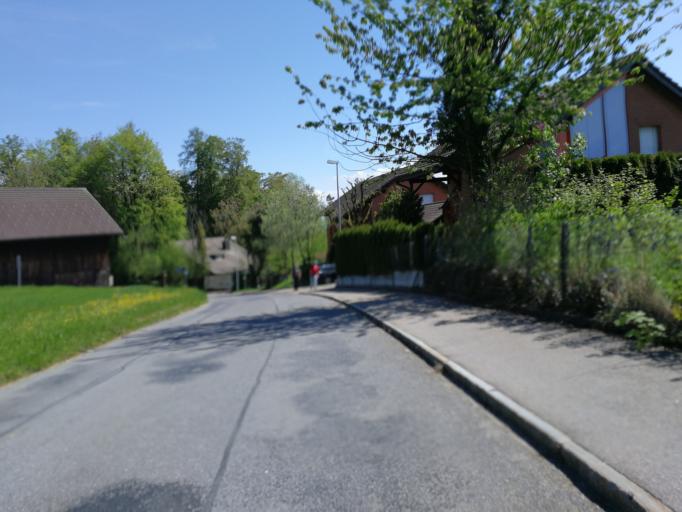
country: CH
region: Zurich
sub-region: Bezirk Meilen
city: Uetikon / Grossdorf
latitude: 47.2729
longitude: 8.6773
